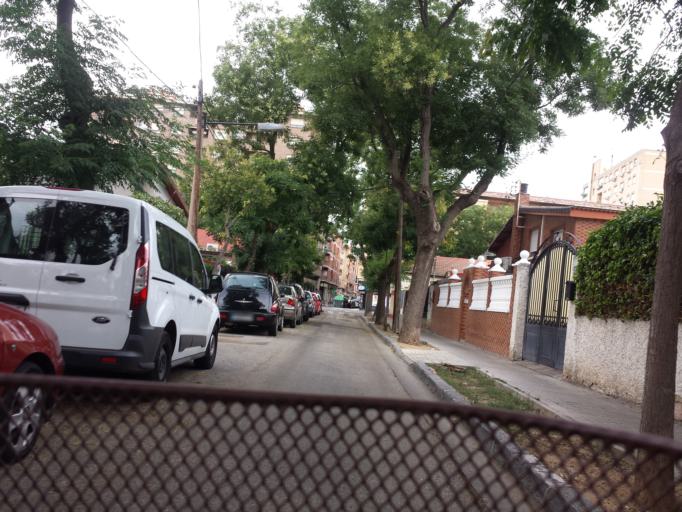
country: ES
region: Aragon
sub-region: Provincia de Zaragoza
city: Delicias
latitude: 41.6474
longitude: -0.9027
